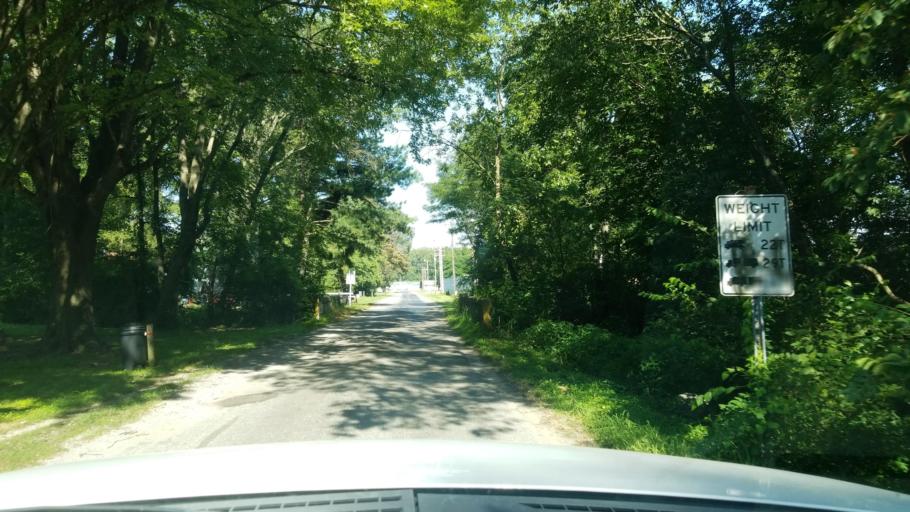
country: US
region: Illinois
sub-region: Saline County
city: Eldorado
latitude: 37.8050
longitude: -88.4602
